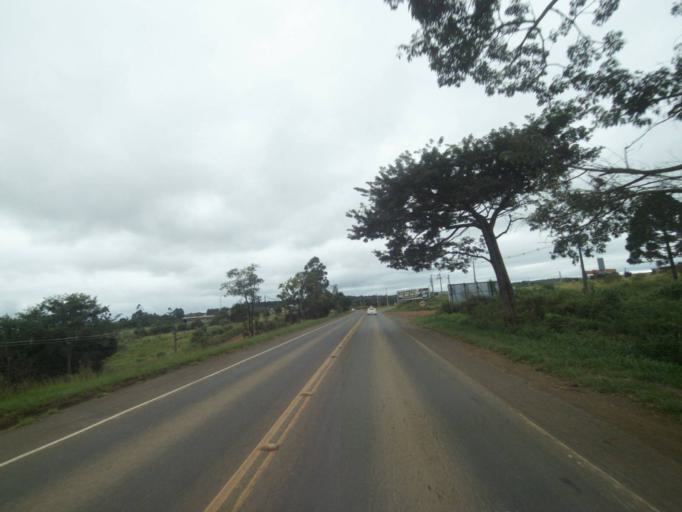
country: BR
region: Parana
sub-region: Telemaco Borba
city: Telemaco Borba
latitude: -24.3855
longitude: -50.6778
